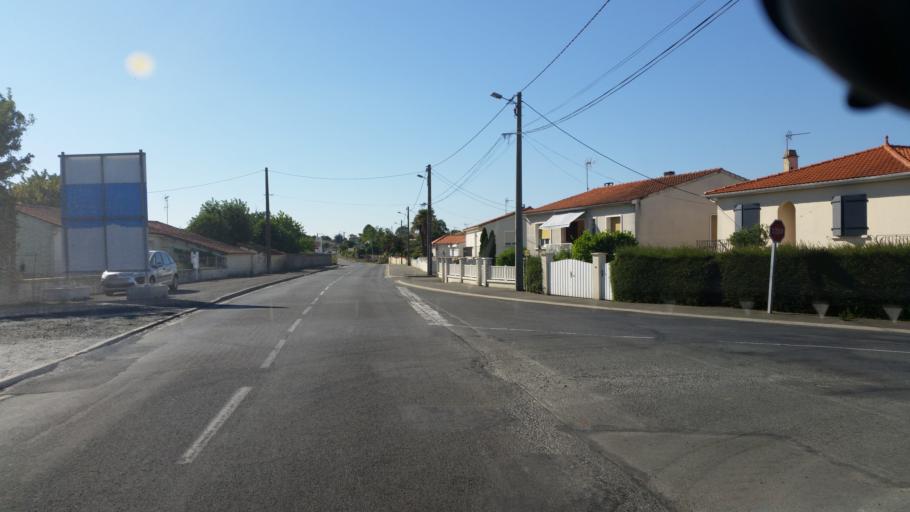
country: FR
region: Poitou-Charentes
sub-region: Departement de la Charente-Maritime
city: Marans
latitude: 46.3023
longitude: -0.9838
